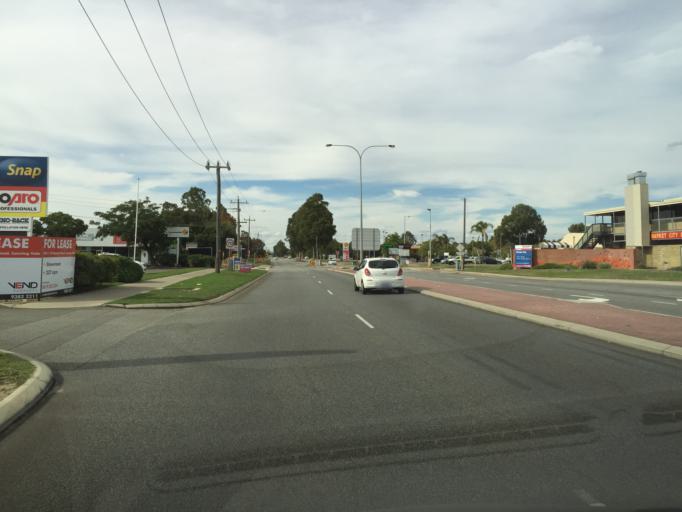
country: AU
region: Western Australia
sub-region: Canning
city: Willetton
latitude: -32.0715
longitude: 115.8934
